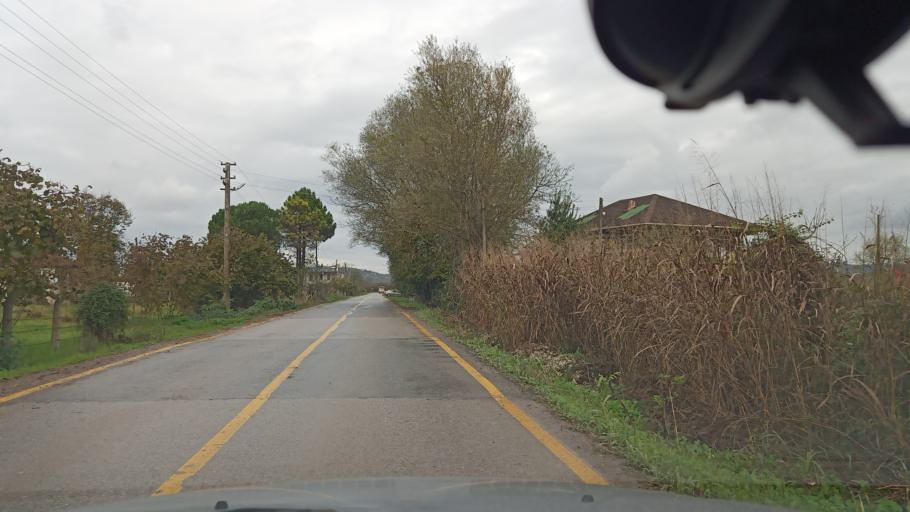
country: TR
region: Sakarya
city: Ortakoy
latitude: 41.0375
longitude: 30.5983
